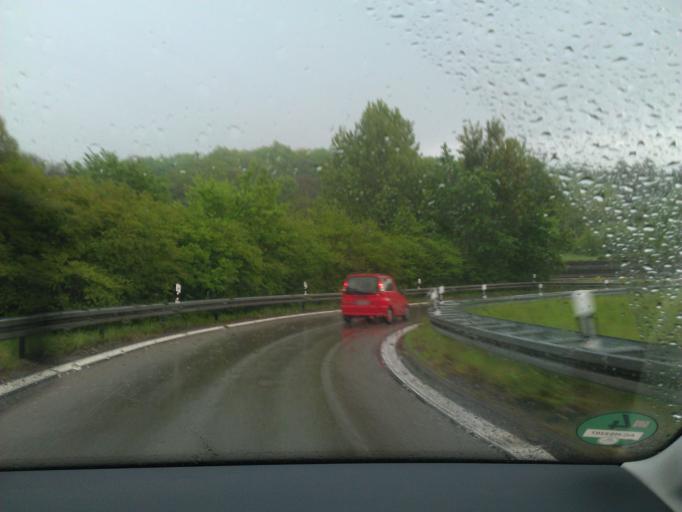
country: DE
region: North Rhine-Westphalia
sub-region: Regierungsbezirk Koln
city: Bayenthal
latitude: 50.8869
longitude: 6.9699
